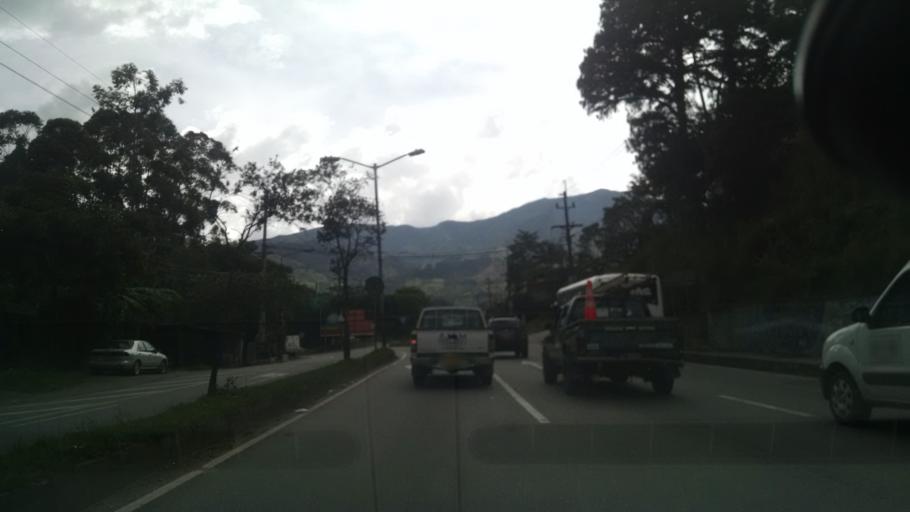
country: CO
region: Antioquia
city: La Estrella
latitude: 6.1532
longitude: -75.6311
